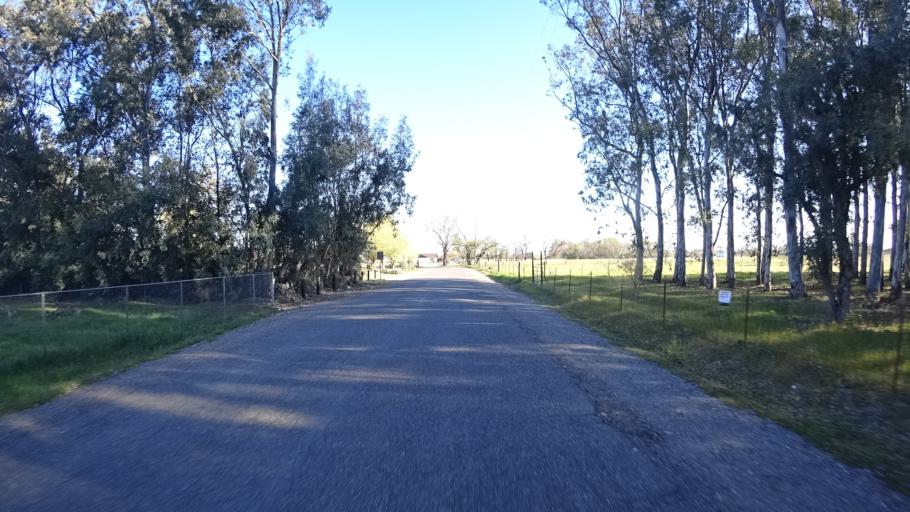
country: US
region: California
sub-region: Glenn County
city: Orland
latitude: 39.7683
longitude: -122.2154
